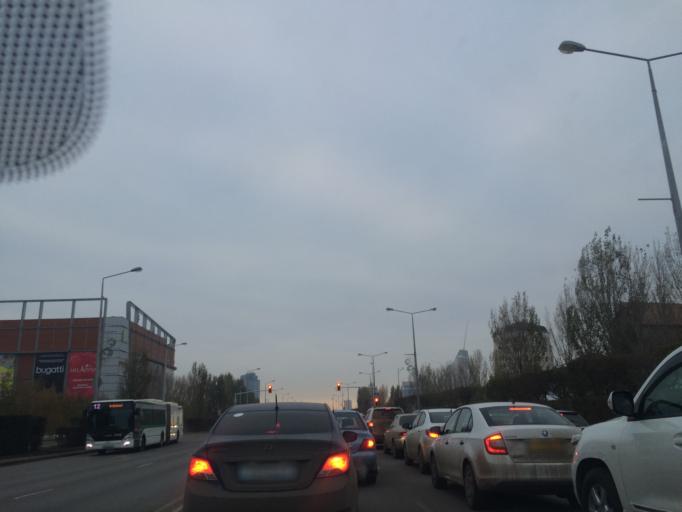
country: KZ
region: Astana Qalasy
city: Astana
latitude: 51.1405
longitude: 71.4099
